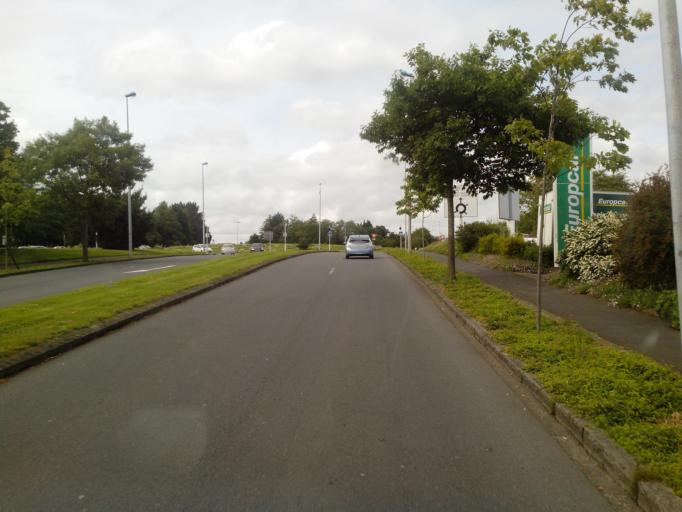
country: FR
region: Brittany
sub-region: Departement du Finistere
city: Brest
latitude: 48.4129
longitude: -4.4804
